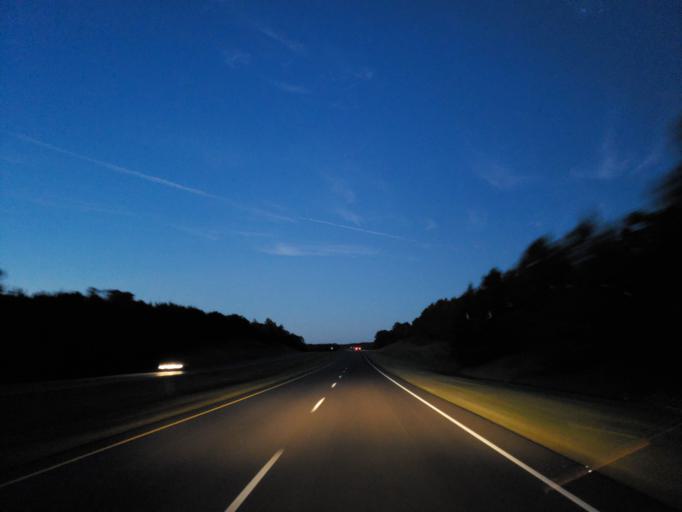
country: US
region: Mississippi
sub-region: Clarke County
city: Quitman
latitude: 32.0250
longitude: -88.6835
